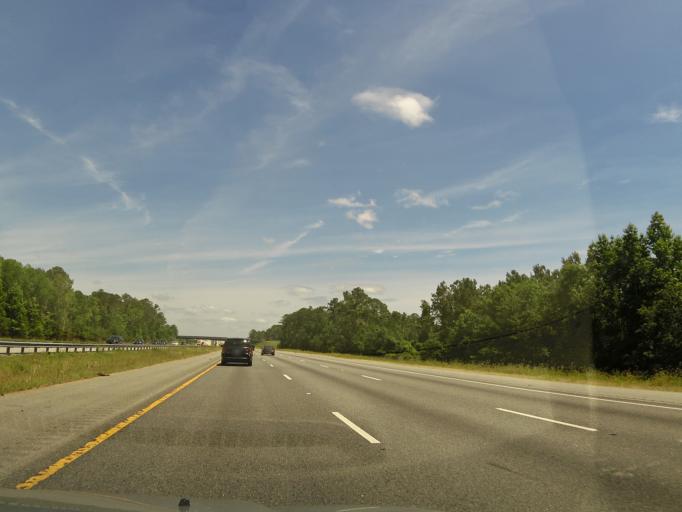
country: US
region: Georgia
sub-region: Glynn County
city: Dock Junction
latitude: 31.1809
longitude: -81.5448
